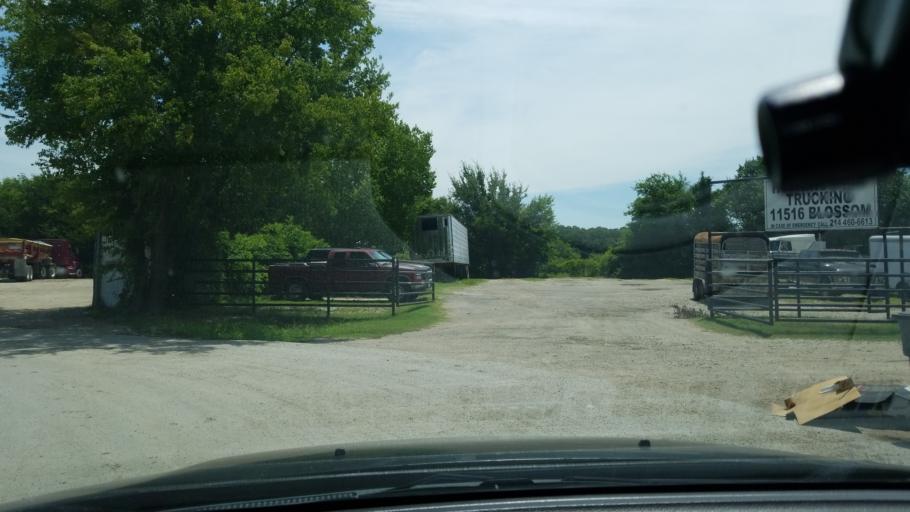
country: US
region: Texas
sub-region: Dallas County
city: Balch Springs
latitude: 32.7436
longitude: -96.6275
